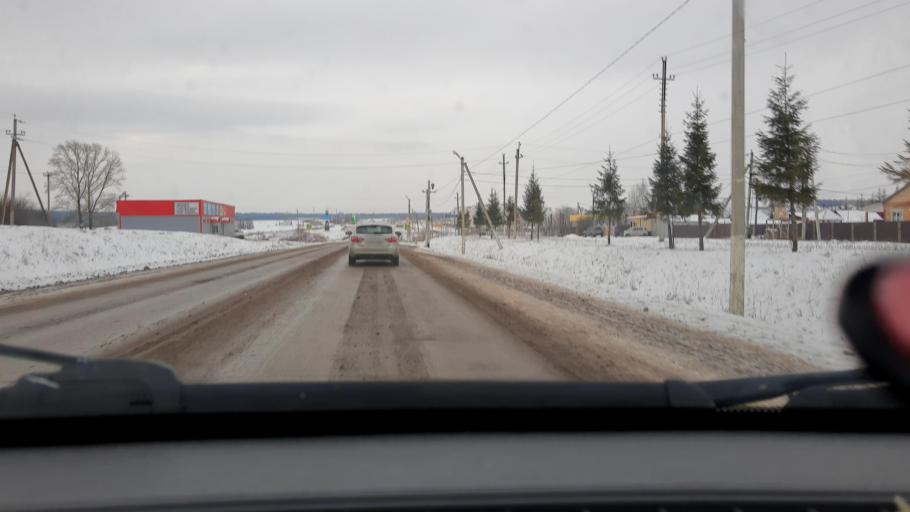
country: RU
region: Bashkortostan
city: Iglino
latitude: 54.8069
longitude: 56.4114
